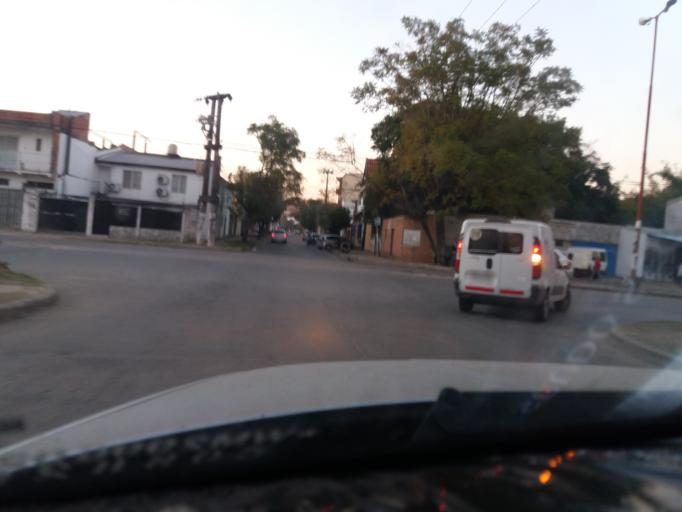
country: AR
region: Corrientes
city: Corrientes
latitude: -27.4849
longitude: -58.8443
